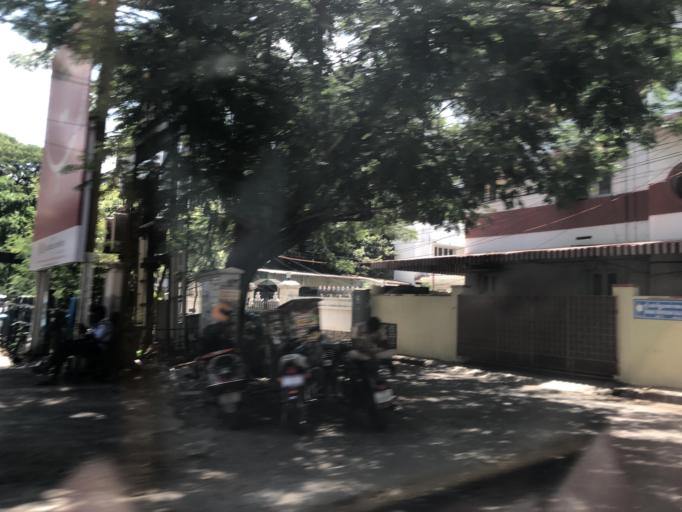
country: IN
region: Tamil Nadu
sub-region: Chennai
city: Chetput
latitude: 13.0406
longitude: 80.2582
